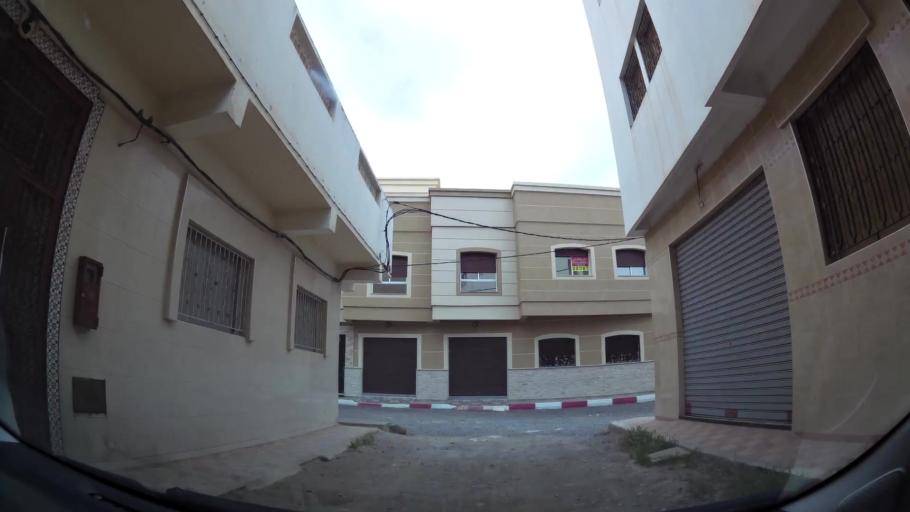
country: MA
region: Oriental
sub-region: Nador
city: Nador
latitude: 35.1583
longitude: -2.9383
